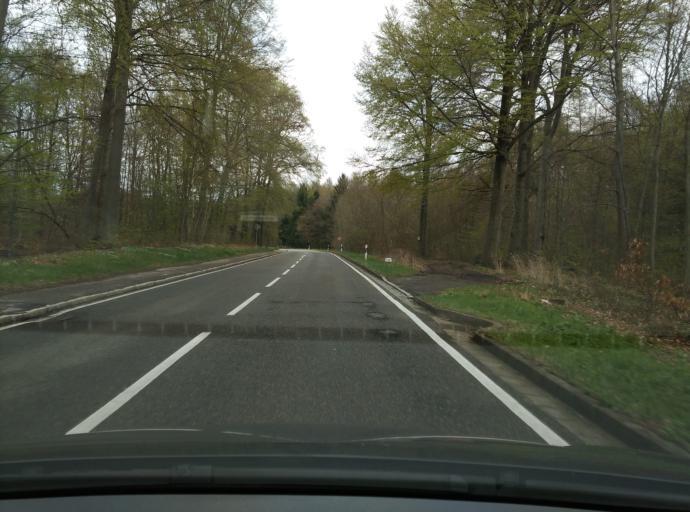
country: DE
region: Baden-Wuerttemberg
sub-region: Regierungsbezirk Stuttgart
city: Kohlberg
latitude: 48.5472
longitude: 9.3127
